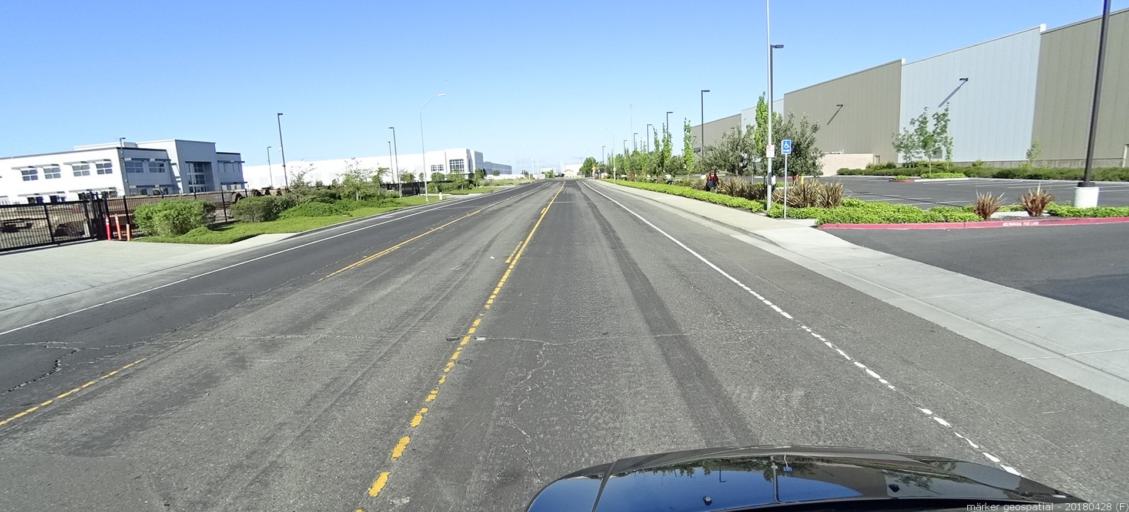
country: US
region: California
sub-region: Yolo County
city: West Sacramento
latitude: 38.5510
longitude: -121.5708
